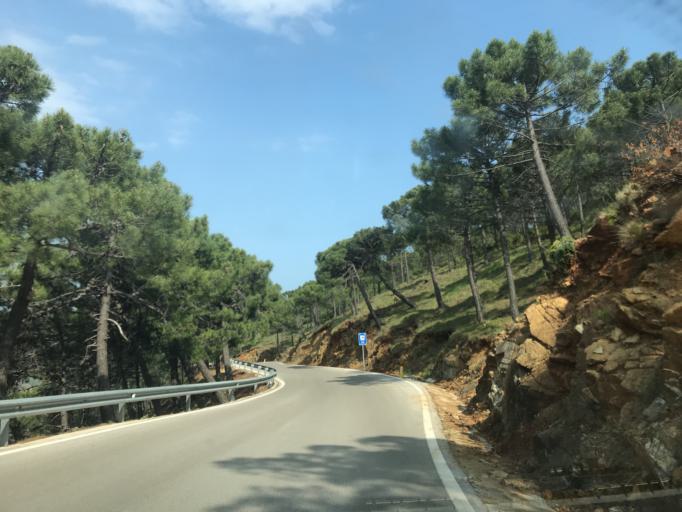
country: ES
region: Andalusia
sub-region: Provincia de Malaga
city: Estepona
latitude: 36.4896
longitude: -5.1836
